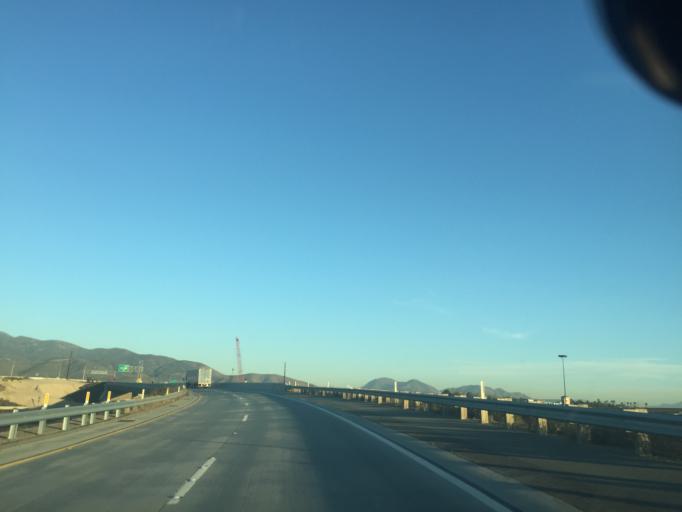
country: MX
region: Baja California
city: Tijuana
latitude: 32.5635
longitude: -116.9515
